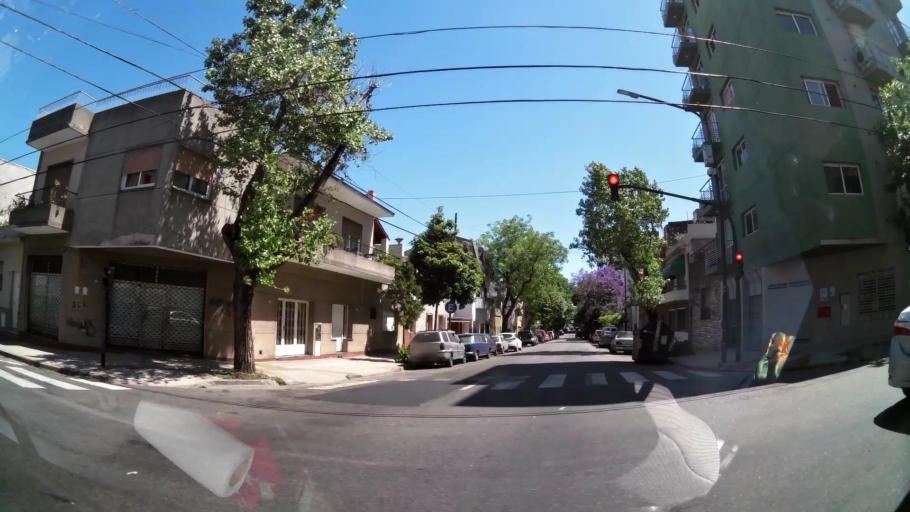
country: AR
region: Buenos Aires F.D.
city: Buenos Aires
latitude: -34.6287
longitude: -58.4099
